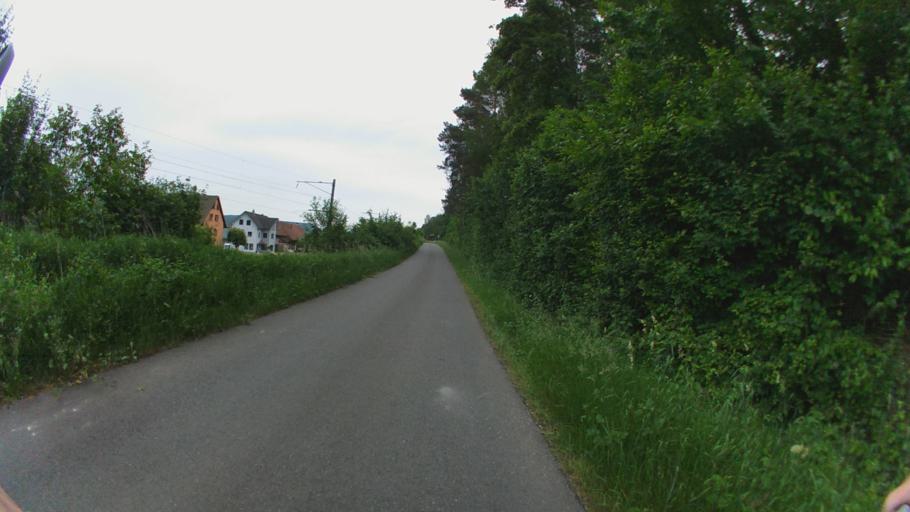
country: CH
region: Aargau
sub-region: Bezirk Zurzach
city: Bad Zurzach
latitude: 47.6031
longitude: 8.2733
